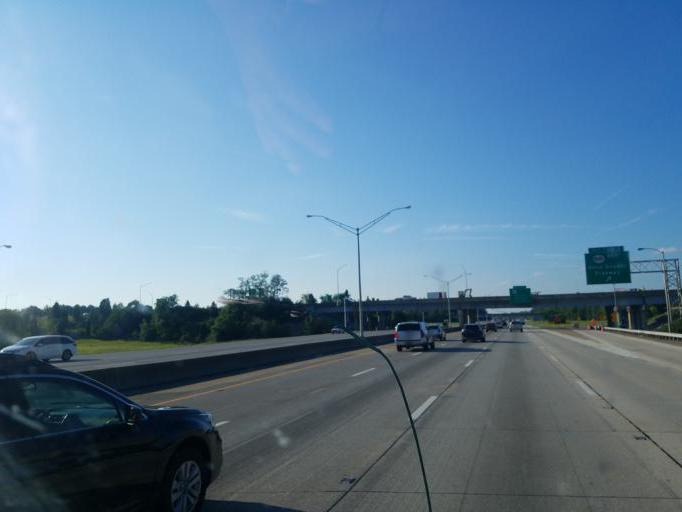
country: US
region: Kentucky
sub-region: Jefferson County
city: Heritage Creek
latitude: 38.1134
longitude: -85.7014
